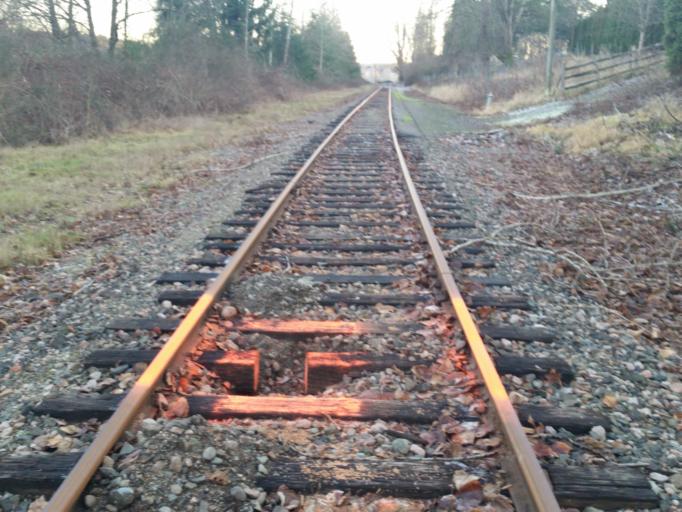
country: US
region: Washington
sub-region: King County
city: Woodinville
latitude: 47.7351
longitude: -122.1523
